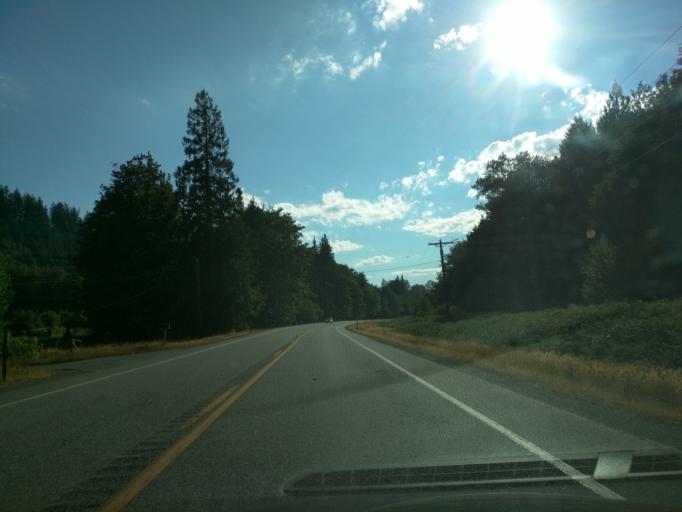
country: US
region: Washington
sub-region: Snohomish County
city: Darrington
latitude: 48.2771
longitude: -121.7867
